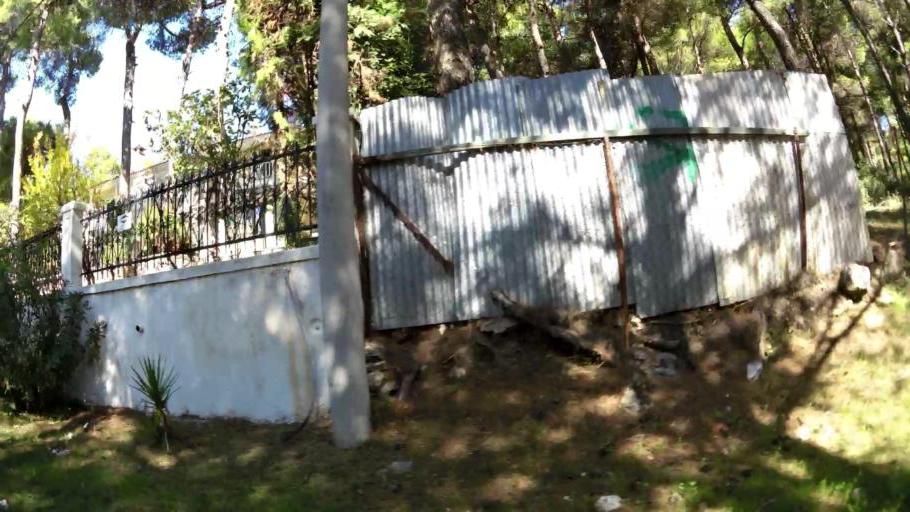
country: GR
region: Attica
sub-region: Nomarchia Anatolikis Attikis
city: Dionysos
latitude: 38.1044
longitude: 23.8808
